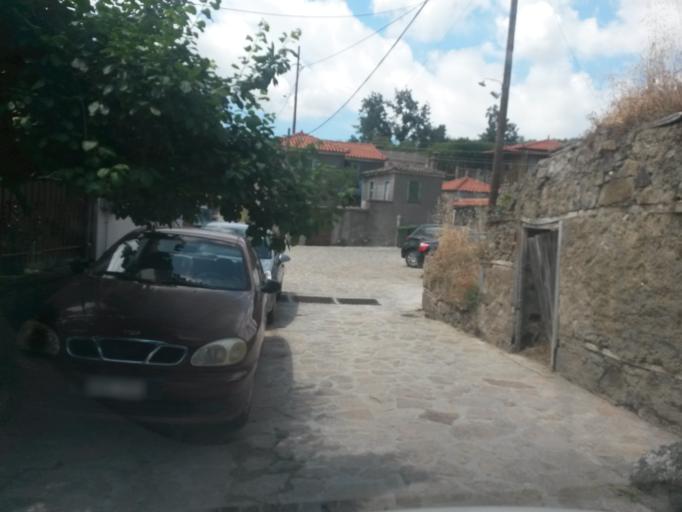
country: GR
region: North Aegean
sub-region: Nomos Lesvou
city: Eresos
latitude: 39.2269
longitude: 26.0521
